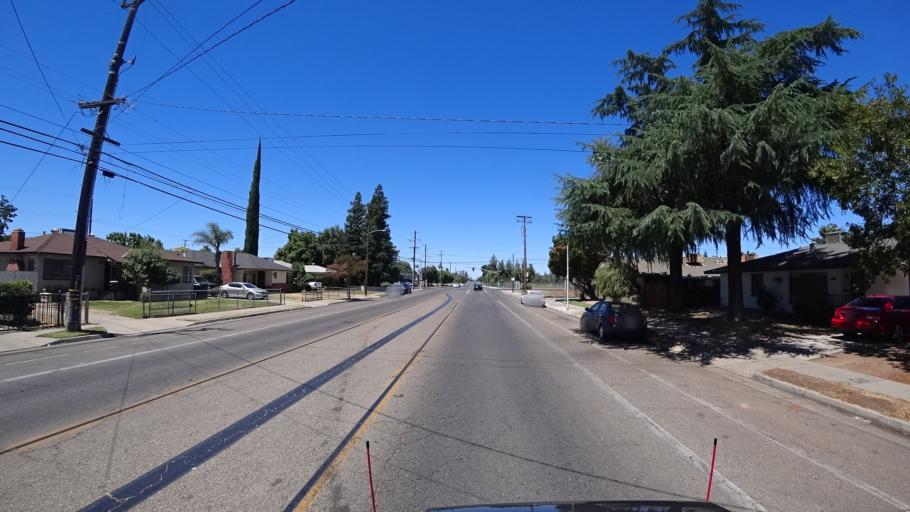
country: US
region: California
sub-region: Fresno County
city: Fresno
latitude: 36.7866
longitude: -119.8163
